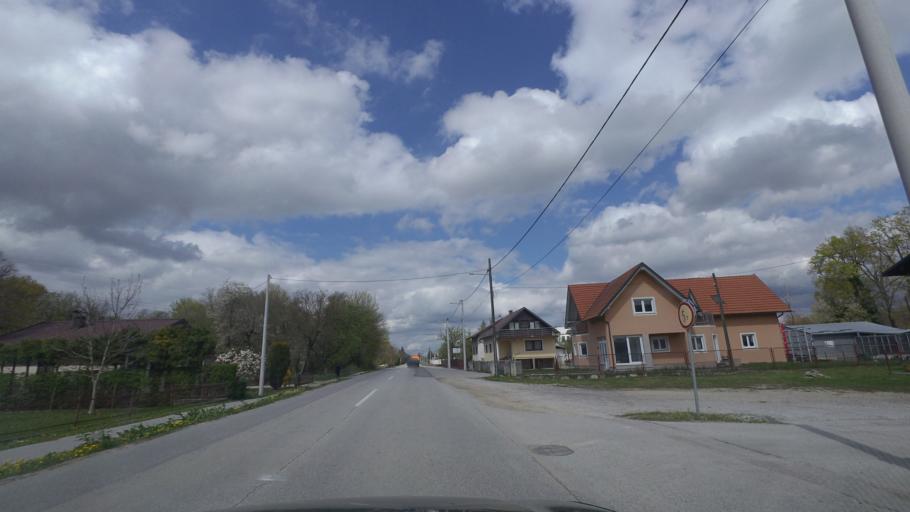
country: HR
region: Zagrebacka
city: Kerestinec
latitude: 45.7567
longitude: 15.8081
